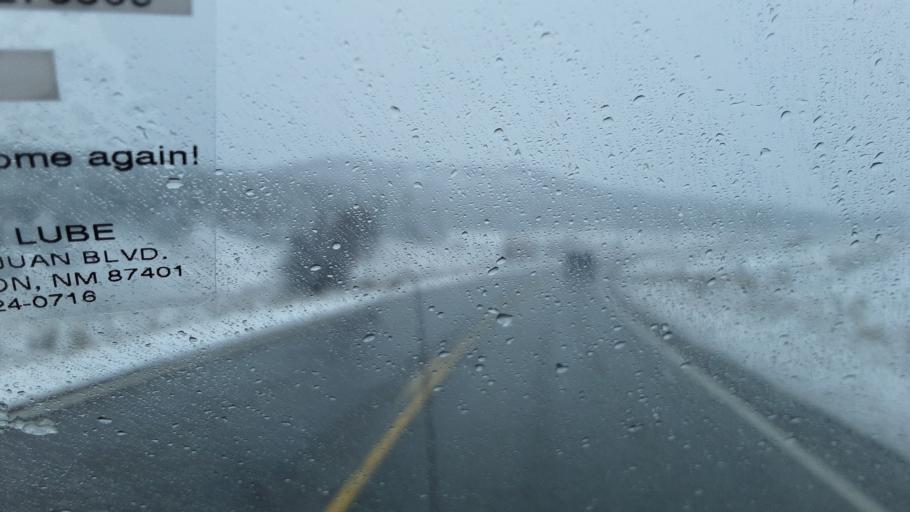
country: US
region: Colorado
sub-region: Archuleta County
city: Pagosa Springs
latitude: 37.2539
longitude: -106.9947
